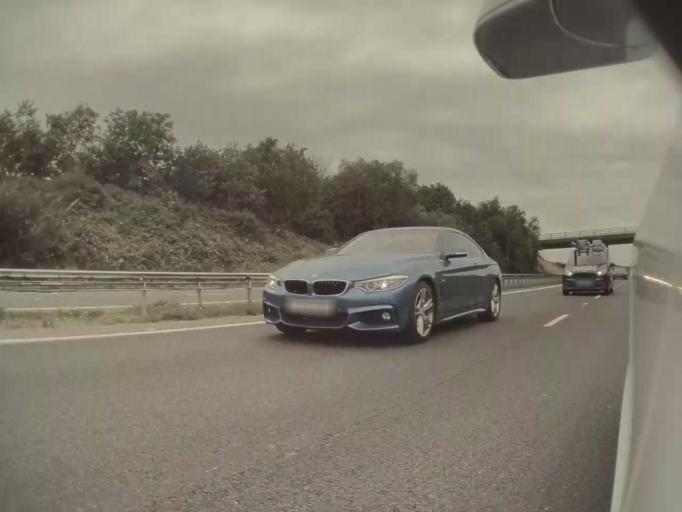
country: GB
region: Wales
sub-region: Anglesey
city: Llanfachraeth
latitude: 53.2567
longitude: -4.4406
